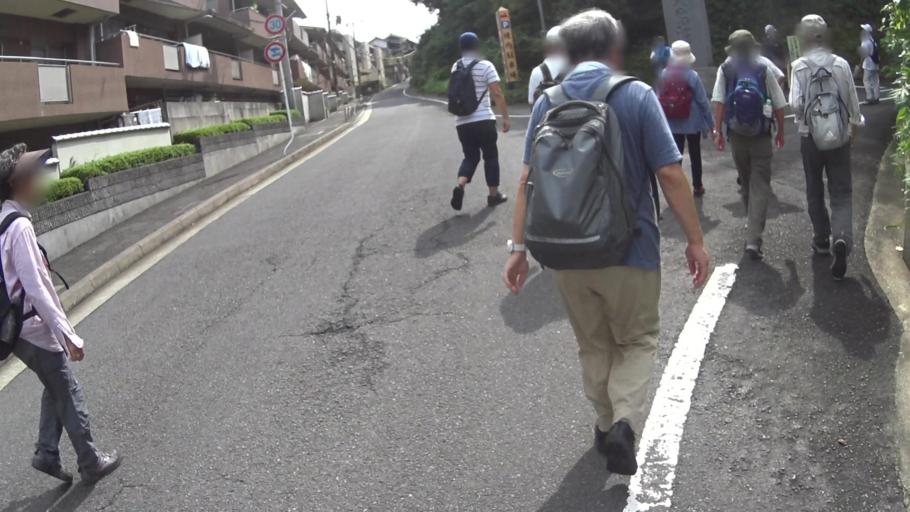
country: JP
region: Nara
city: Sakurai
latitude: 34.5041
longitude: 135.8429
